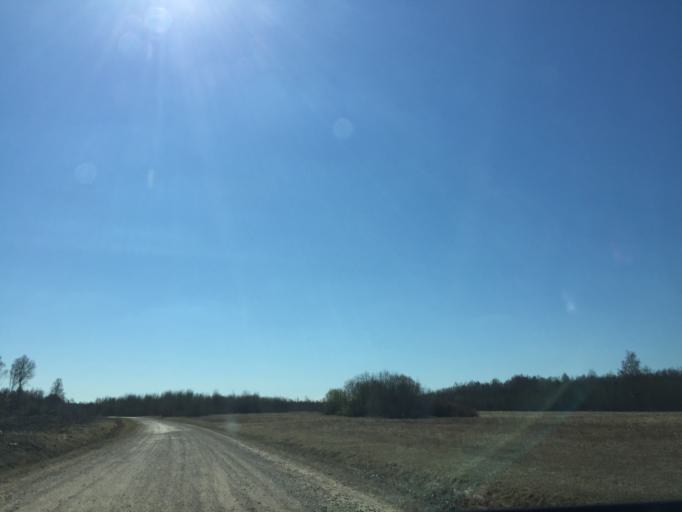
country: EE
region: Viljandimaa
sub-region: Viiratsi vald
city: Viiratsi
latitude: 58.4023
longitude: 25.8709
